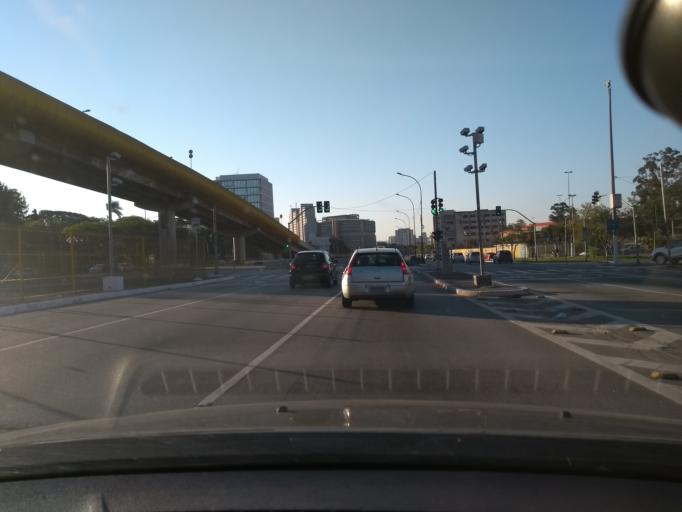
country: BR
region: Sao Paulo
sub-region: Sao Paulo
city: Sao Paulo
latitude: -23.5639
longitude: -46.6112
